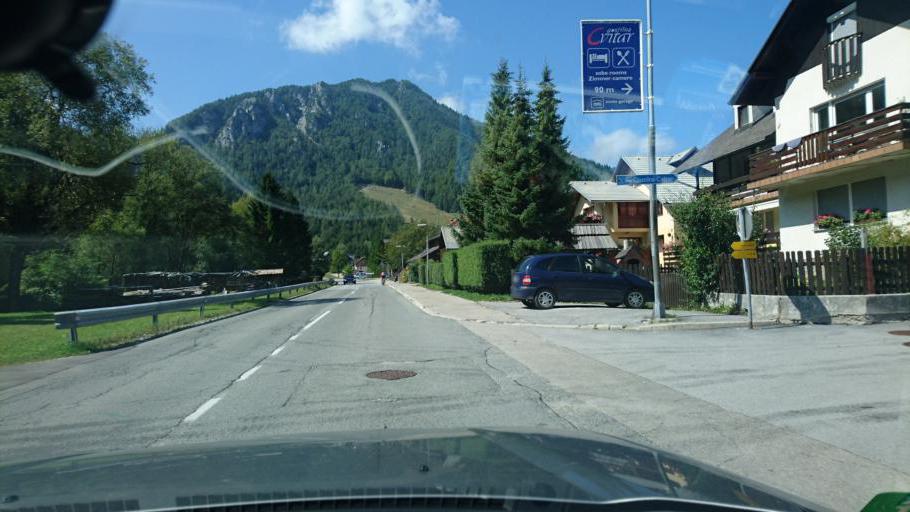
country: SI
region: Kranjska Gora
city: Kranjska Gora
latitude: 46.4834
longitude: 13.7861
